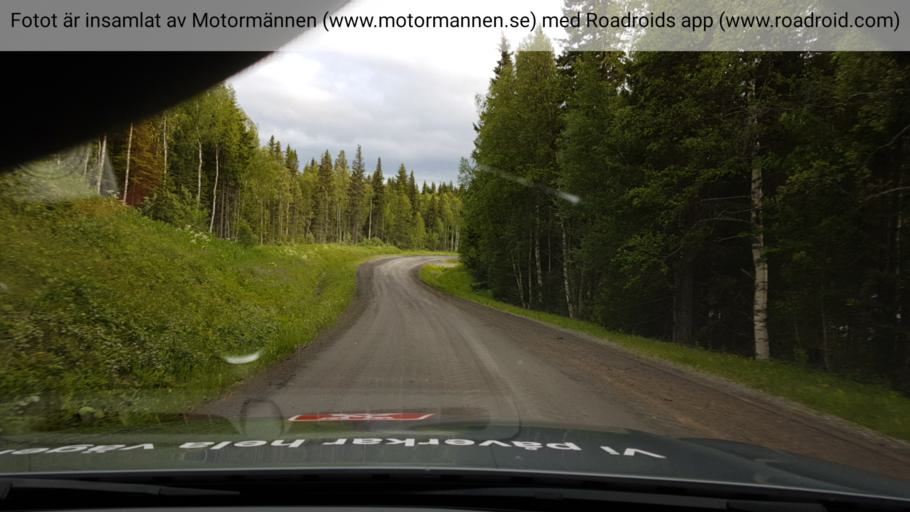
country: SE
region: Jaemtland
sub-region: OEstersunds Kommun
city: Lit
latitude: 63.5788
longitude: 14.9812
